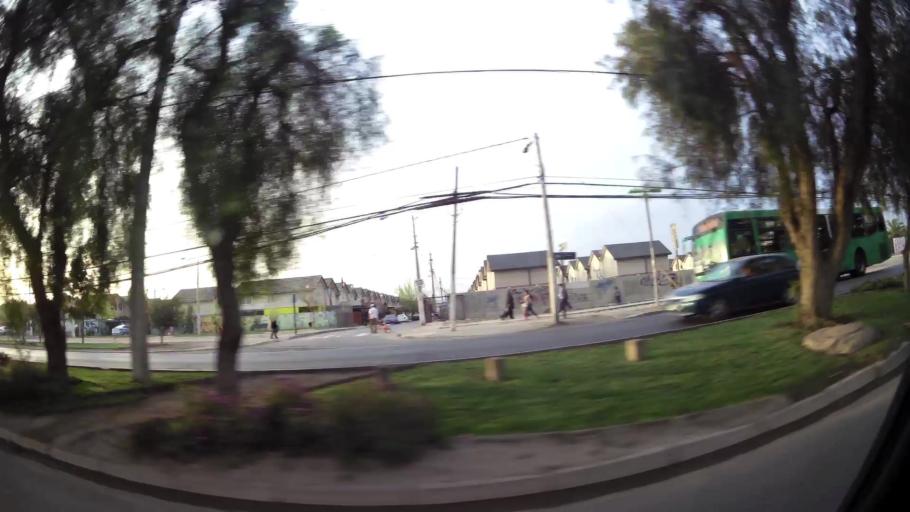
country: CL
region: Santiago Metropolitan
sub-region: Provincia de Santiago
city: Lo Prado
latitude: -33.5063
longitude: -70.7940
